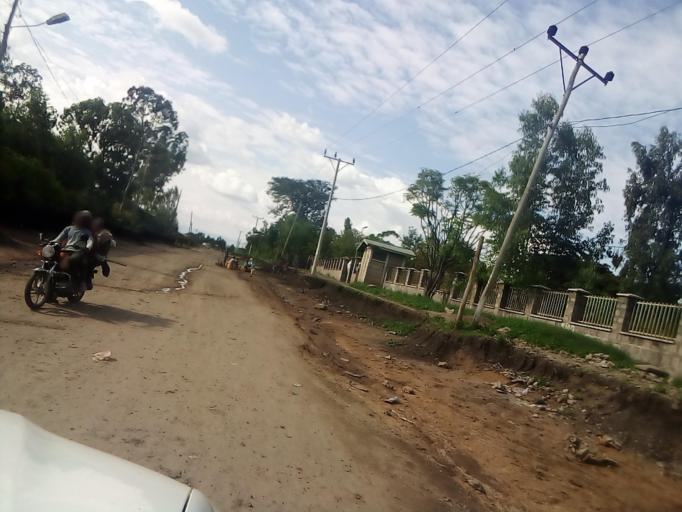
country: ET
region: Southern Nations, Nationalities, and People's Region
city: K'olito
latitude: 7.5956
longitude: 38.0680
